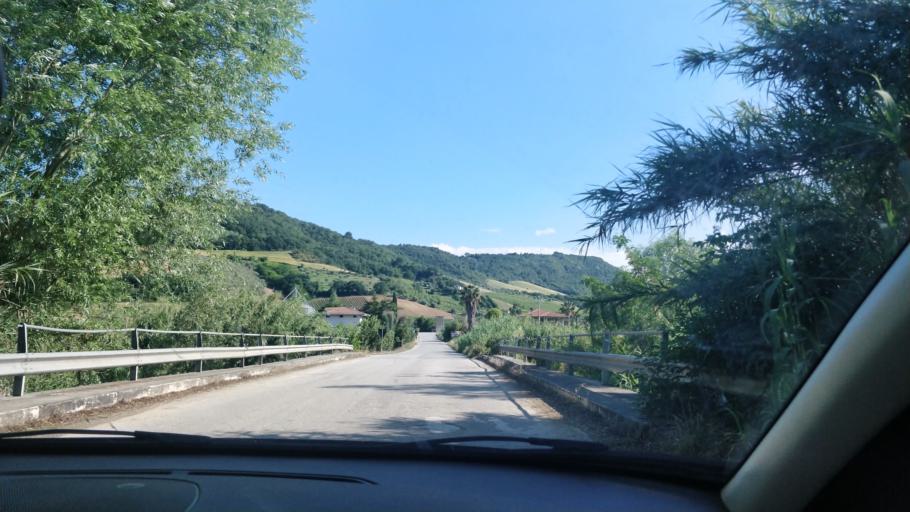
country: IT
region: The Marches
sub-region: Provincia di Ascoli Piceno
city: Massignano
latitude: 43.0368
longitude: 13.8003
